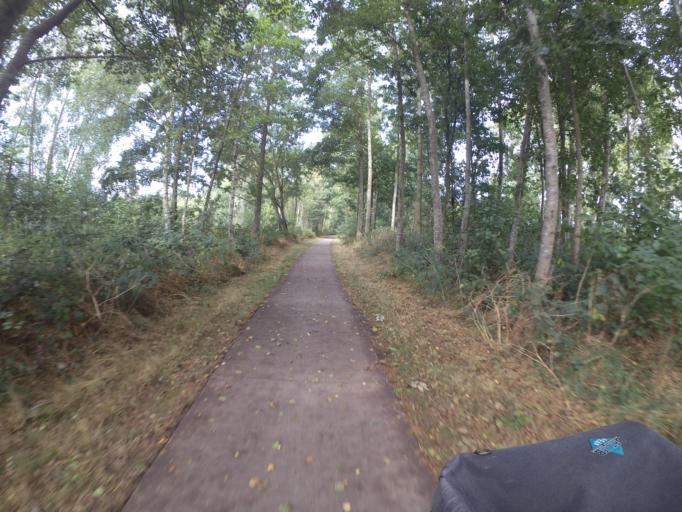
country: NL
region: Gelderland
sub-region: Gemeente Brummen
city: Eerbeek
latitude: 52.1607
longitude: 6.0580
